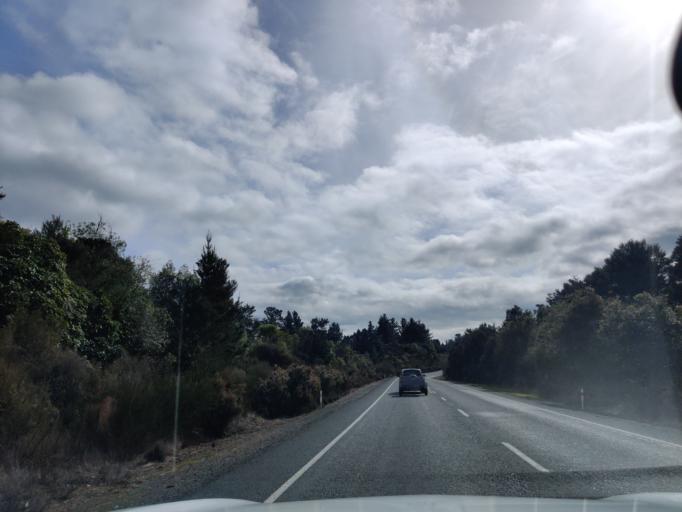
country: NZ
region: Waikato
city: Turangi
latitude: -39.0285
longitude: 175.8110
